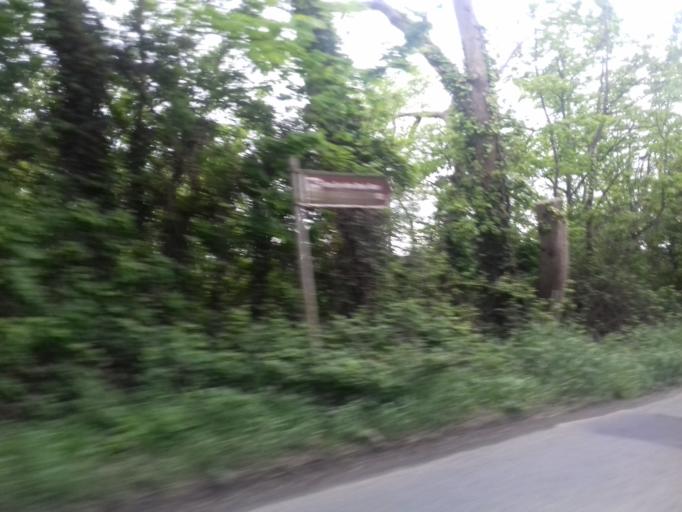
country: IE
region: Leinster
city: Donabate
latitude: 53.4919
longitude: -6.1798
